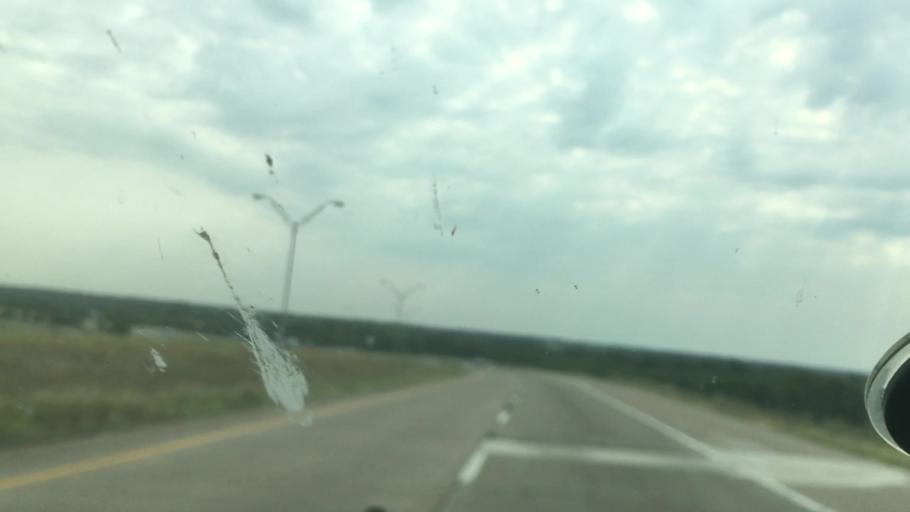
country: US
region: Texas
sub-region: Grayson County
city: Denison
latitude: 33.8003
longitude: -96.5404
